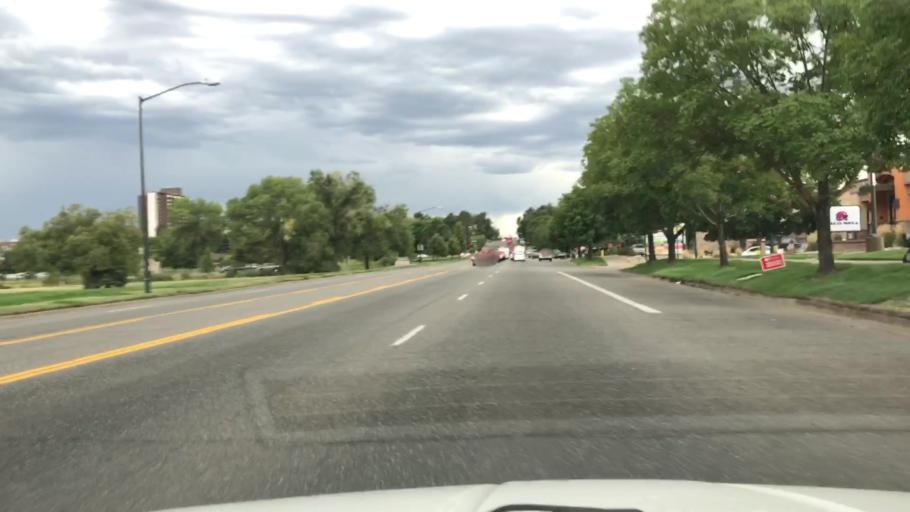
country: US
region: Colorado
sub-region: Jefferson County
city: Edgewater
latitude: 39.7471
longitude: -105.0533
